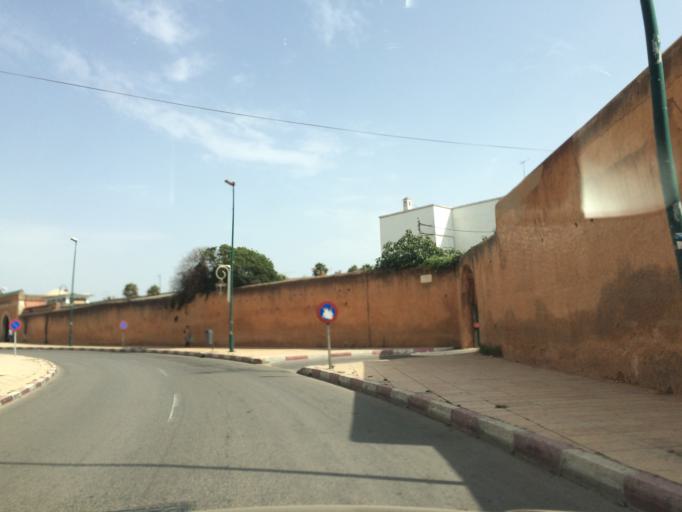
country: MA
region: Rabat-Sale-Zemmour-Zaer
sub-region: Rabat
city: Rabat
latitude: 34.0133
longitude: -6.8336
